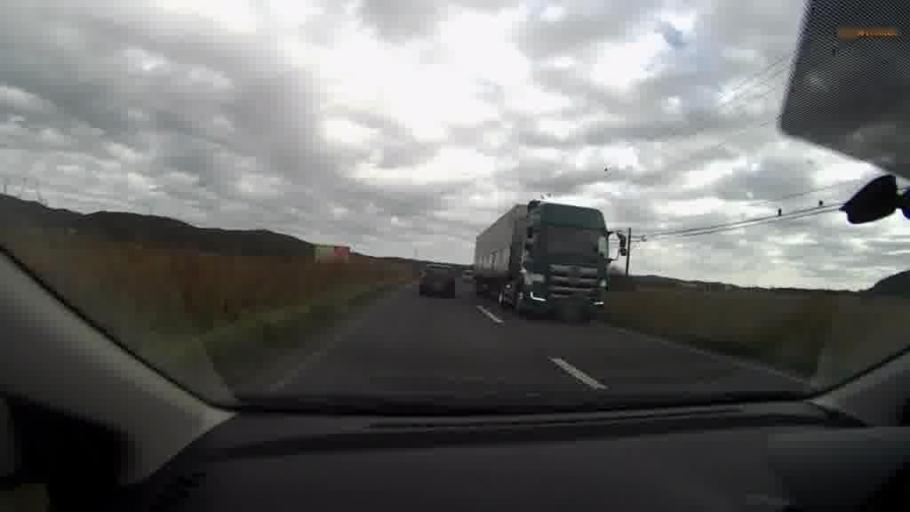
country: JP
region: Hokkaido
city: Kushiro
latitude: 42.9468
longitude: 144.0370
